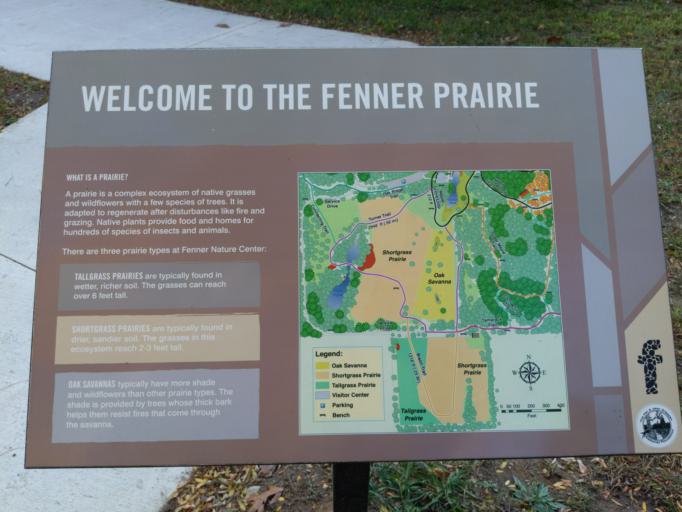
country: US
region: Michigan
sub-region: Ingham County
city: Lansing
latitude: 42.7090
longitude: -84.5196
